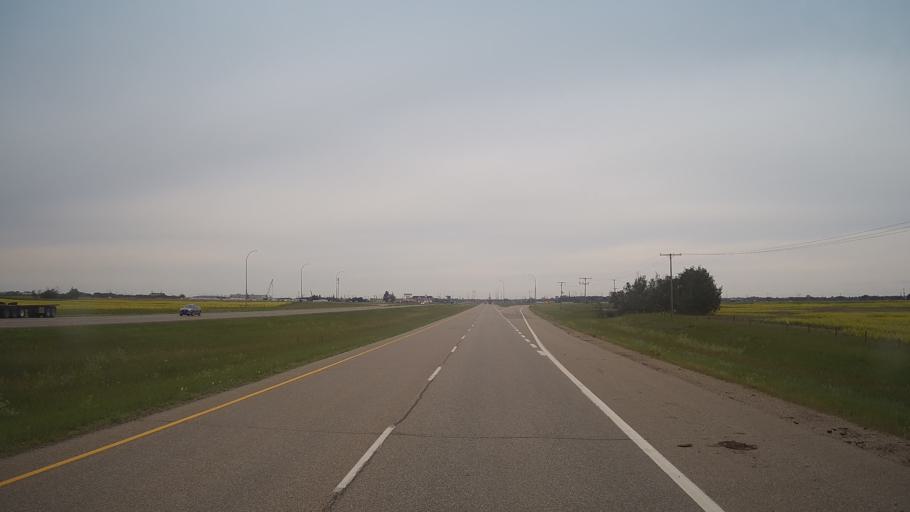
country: CA
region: Saskatchewan
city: Saskatoon
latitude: 52.0467
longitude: -106.5930
